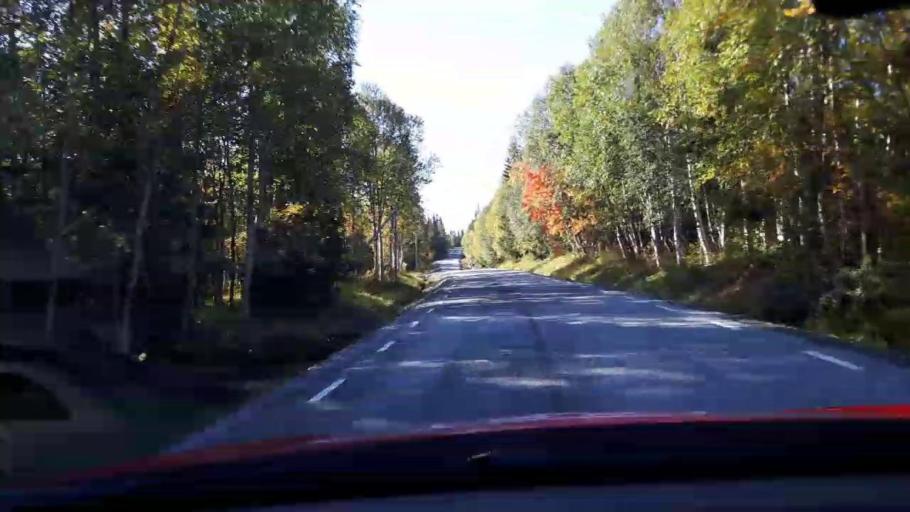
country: NO
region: Nord-Trondelag
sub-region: Royrvik
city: Royrvik
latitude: 64.8162
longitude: 14.2091
